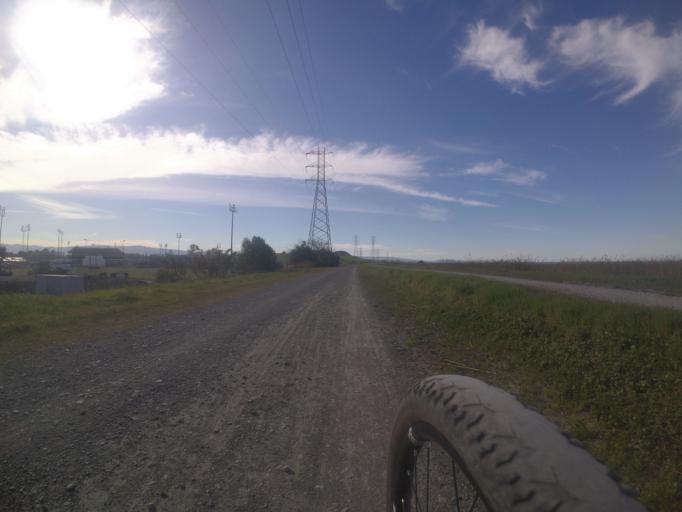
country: US
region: California
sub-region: Santa Clara County
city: Sunnyvale
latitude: 37.4176
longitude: -121.9989
